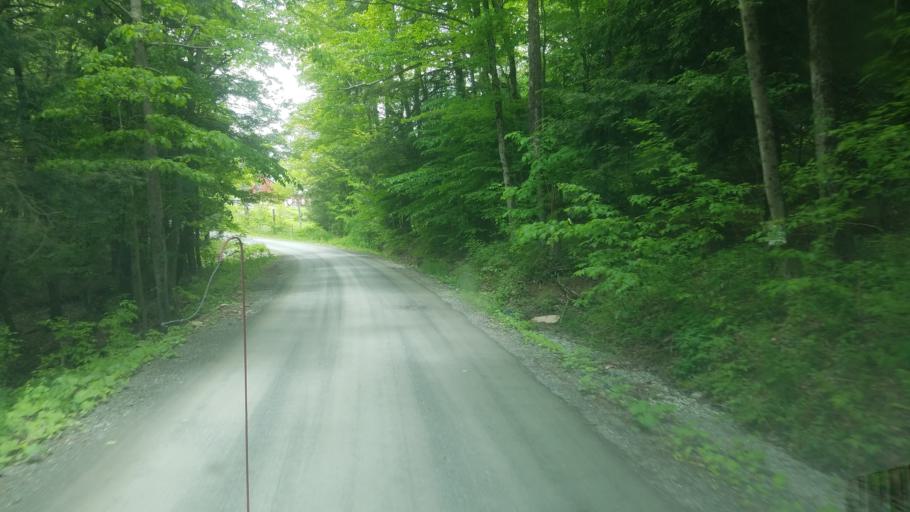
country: US
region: Pennsylvania
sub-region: Tioga County
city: Westfield
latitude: 41.8501
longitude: -77.6034
